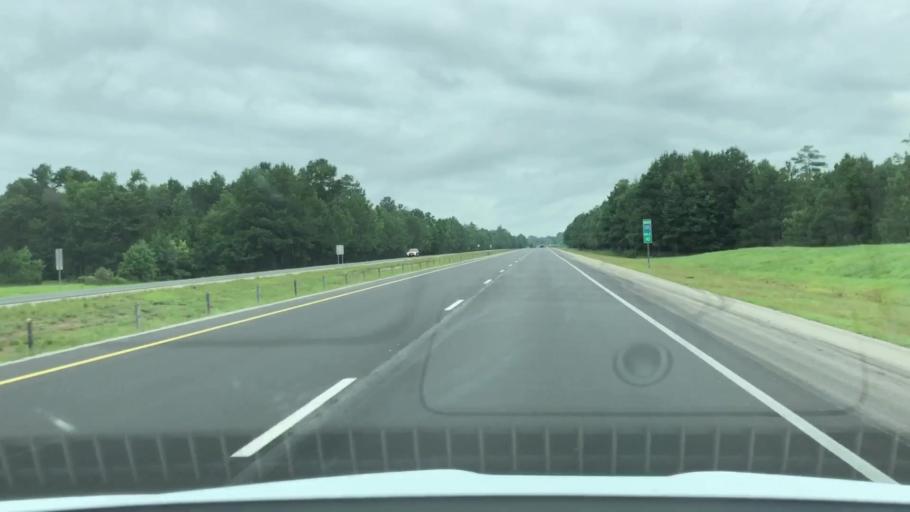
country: US
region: North Carolina
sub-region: Wilson County
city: Lucama
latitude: 35.6094
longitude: -77.9799
